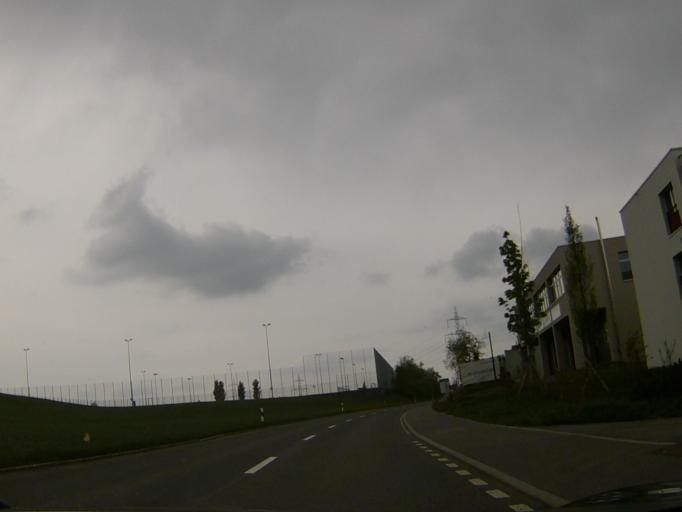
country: CH
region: Zug
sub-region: Zug
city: Menzingen
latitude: 47.1723
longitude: 8.6035
